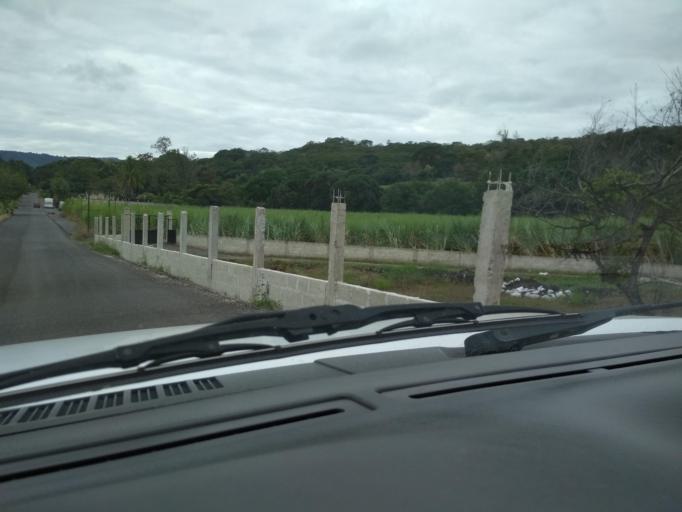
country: MX
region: Veracruz
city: Alto Lucero
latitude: 19.5900
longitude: -96.7880
